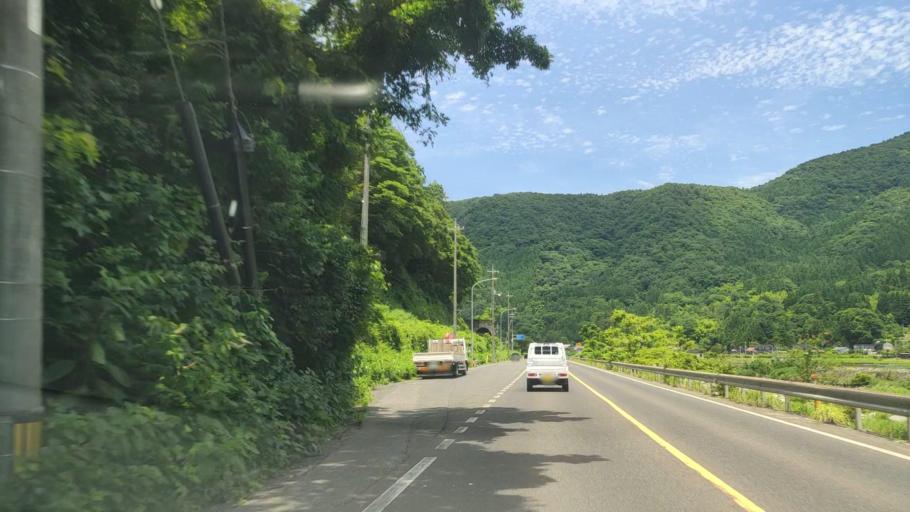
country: JP
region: Tottori
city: Tottori
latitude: 35.3637
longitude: 134.3781
